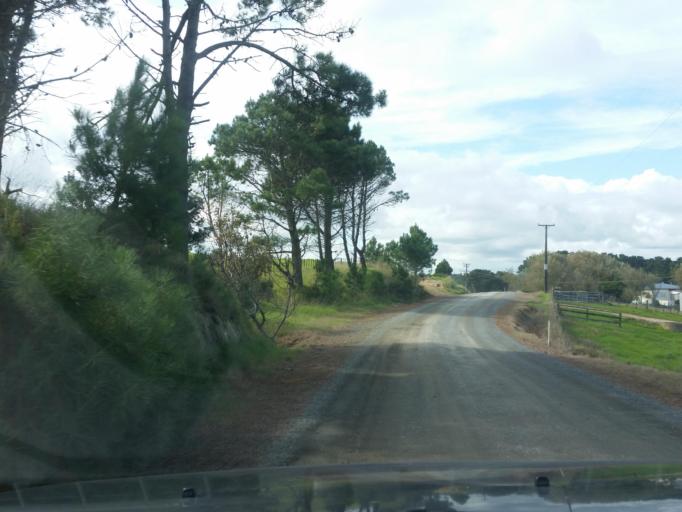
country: NZ
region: Northland
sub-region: Kaipara District
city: Dargaville
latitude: -35.9093
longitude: 173.7821
